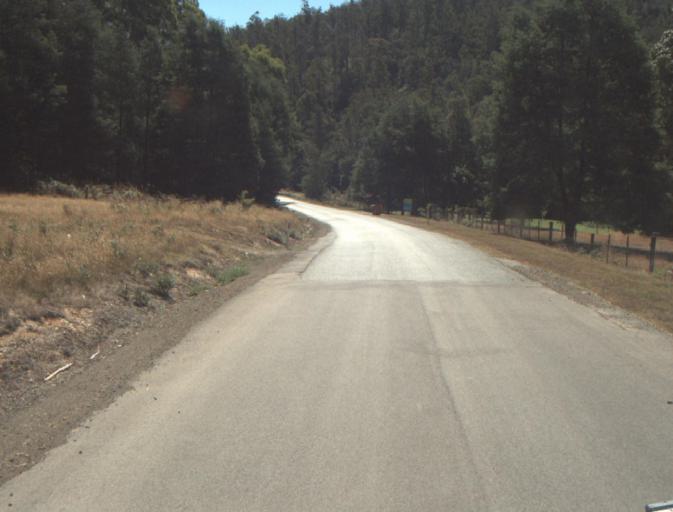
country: AU
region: Tasmania
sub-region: Dorset
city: Scottsdale
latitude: -41.3110
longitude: 147.3983
